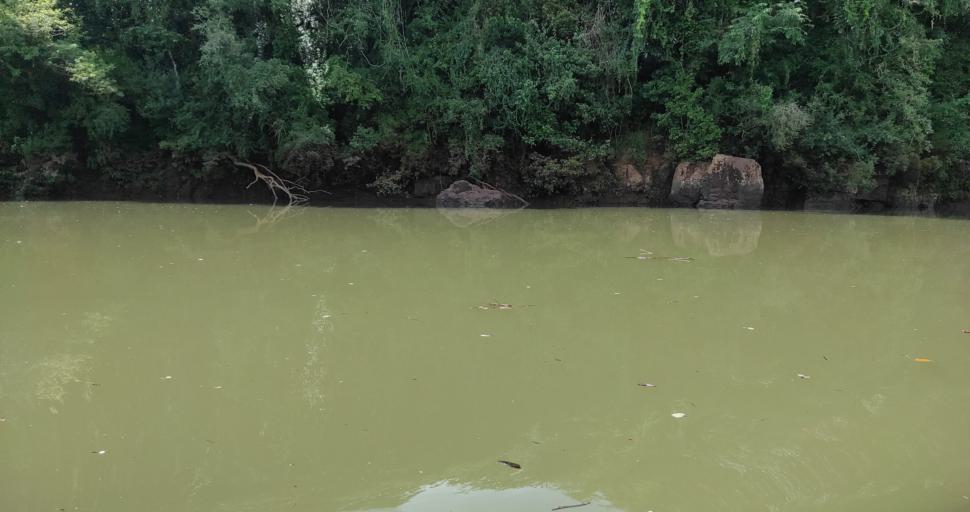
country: AR
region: Misiones
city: El Soberbio
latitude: -27.2839
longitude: -54.1939
